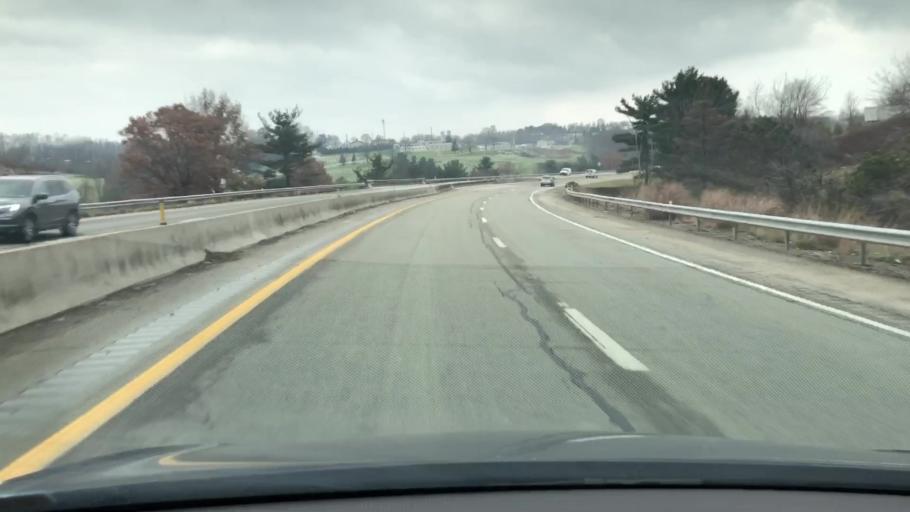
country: US
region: Pennsylvania
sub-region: Fayette County
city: East Uniontown
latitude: 39.9367
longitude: -79.6627
